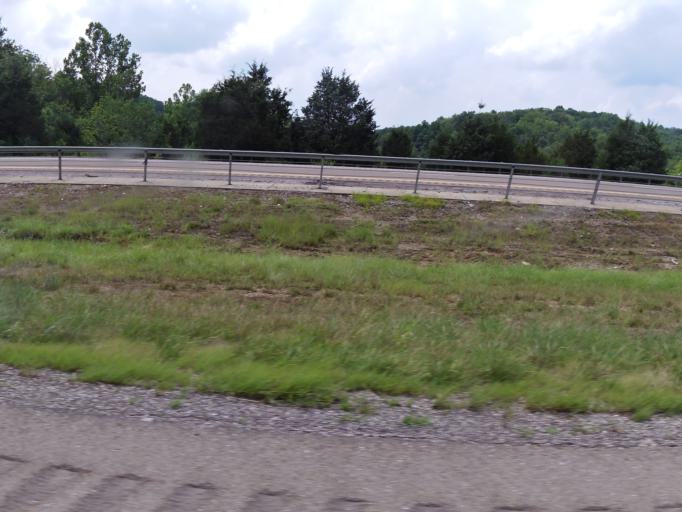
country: US
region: Kentucky
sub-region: Gallatin County
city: Warsaw
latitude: 38.7533
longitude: -84.8086
